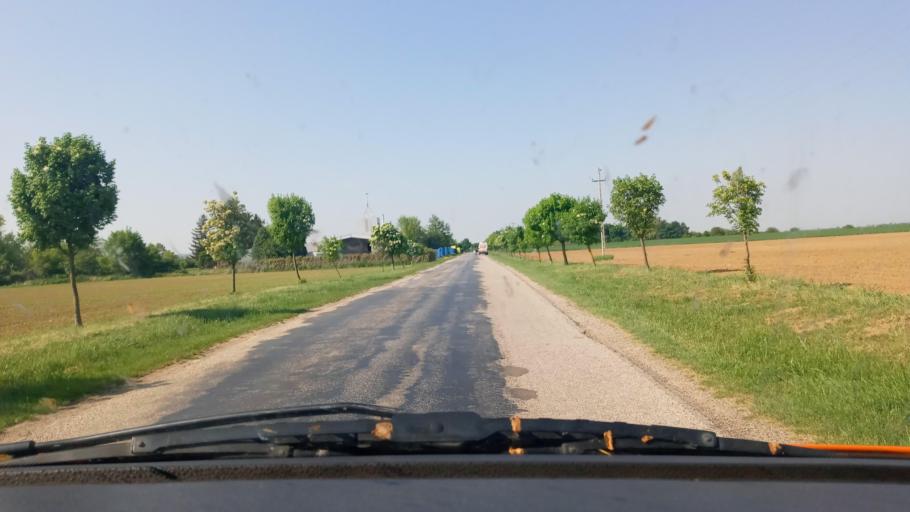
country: HU
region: Baranya
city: Kozarmisleny
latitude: 45.9979
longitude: 18.3169
